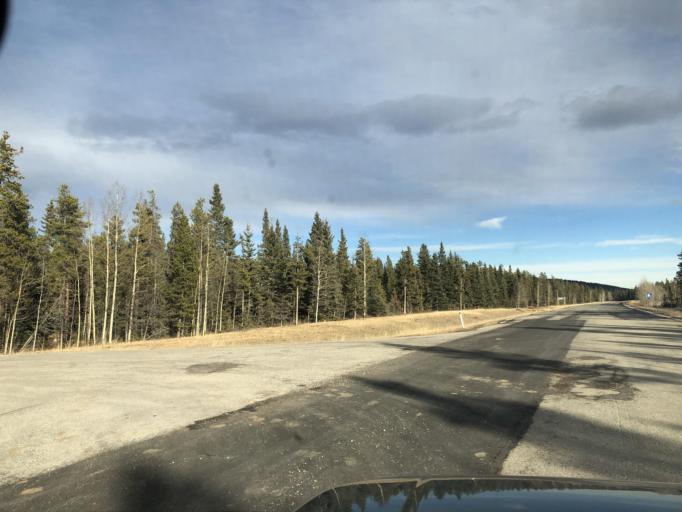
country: CA
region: Alberta
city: Cochrane
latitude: 51.0426
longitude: -114.8612
